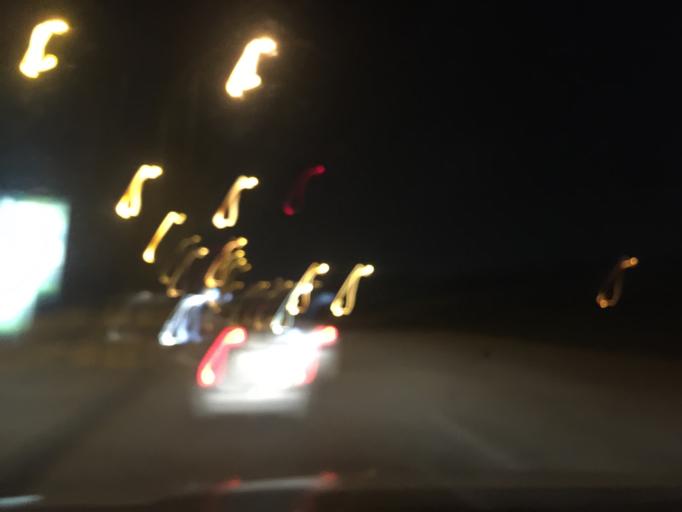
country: JO
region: Amman
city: Umm as Summaq
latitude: 31.9184
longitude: 35.8623
